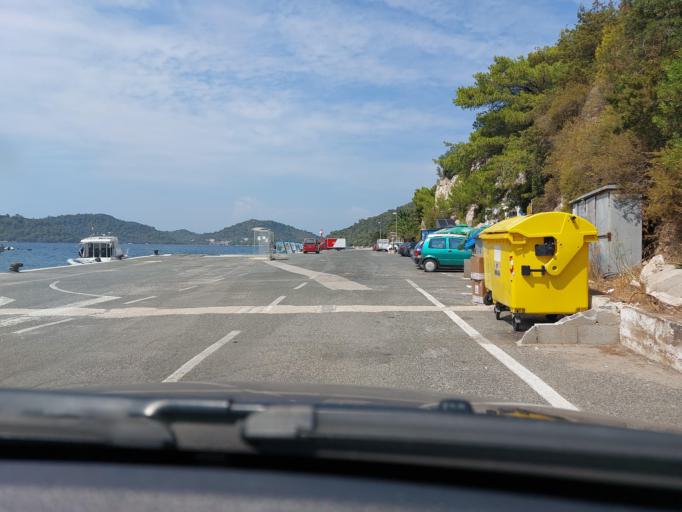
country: HR
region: Dubrovacko-Neretvanska
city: Smokvica
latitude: 42.7449
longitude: 16.8249
